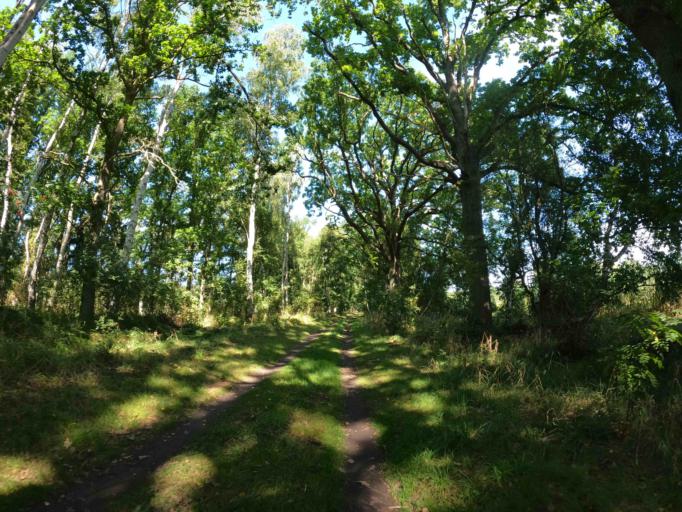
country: DE
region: Mecklenburg-Vorpommern
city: Prohn
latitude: 54.4277
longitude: 13.0307
